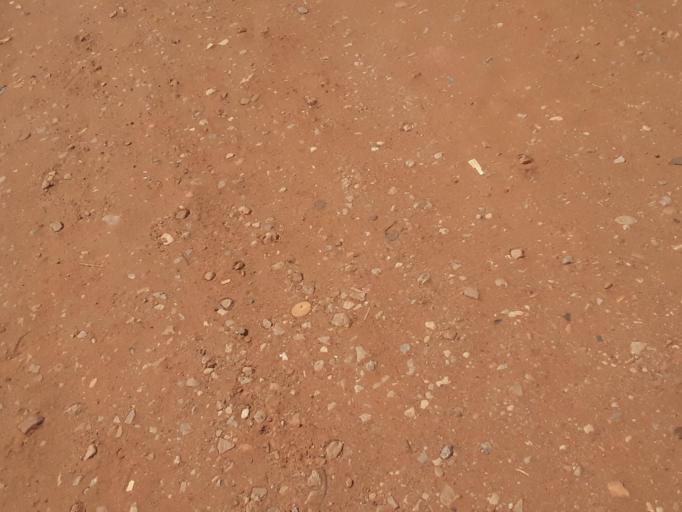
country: ZM
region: Lusaka
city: Lusaka
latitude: -15.3560
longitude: 28.2818
